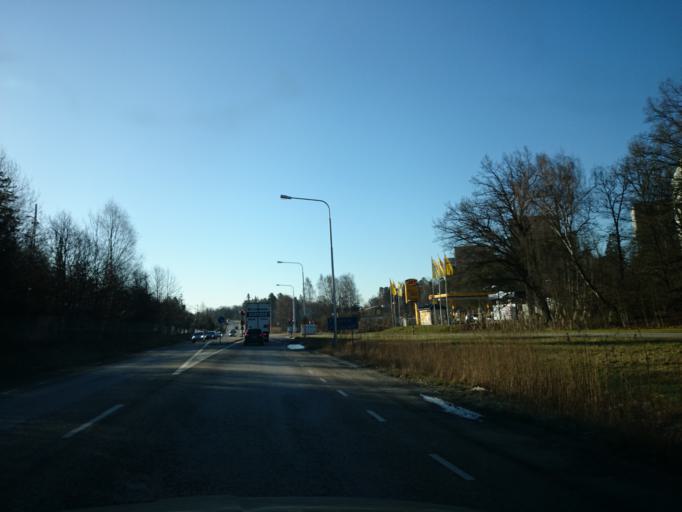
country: SE
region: Stockholm
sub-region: Stockholms Kommun
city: Arsta
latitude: 59.2489
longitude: 18.0637
